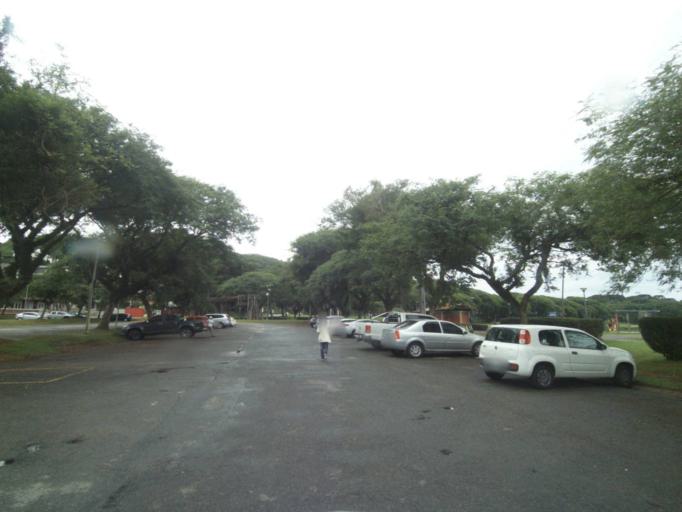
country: BR
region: Parana
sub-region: Curitiba
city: Curitiba
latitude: -25.4299
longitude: -49.3150
